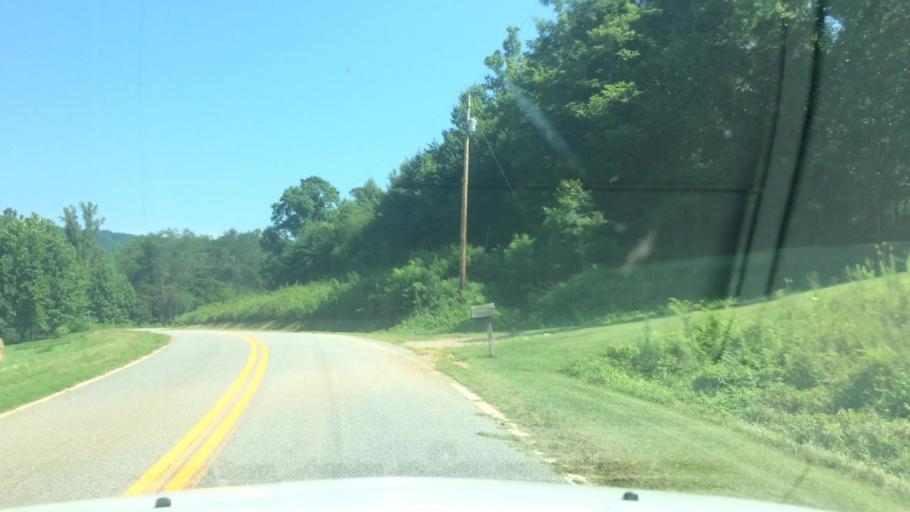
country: US
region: North Carolina
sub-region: Alexander County
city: Taylorsville
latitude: 35.9954
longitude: -81.2696
